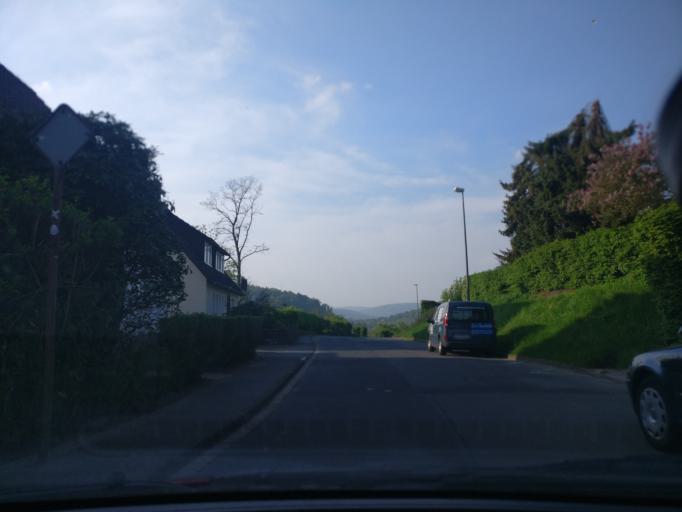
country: DE
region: Lower Saxony
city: Hannoversch Munden
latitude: 51.4044
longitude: 9.6502
